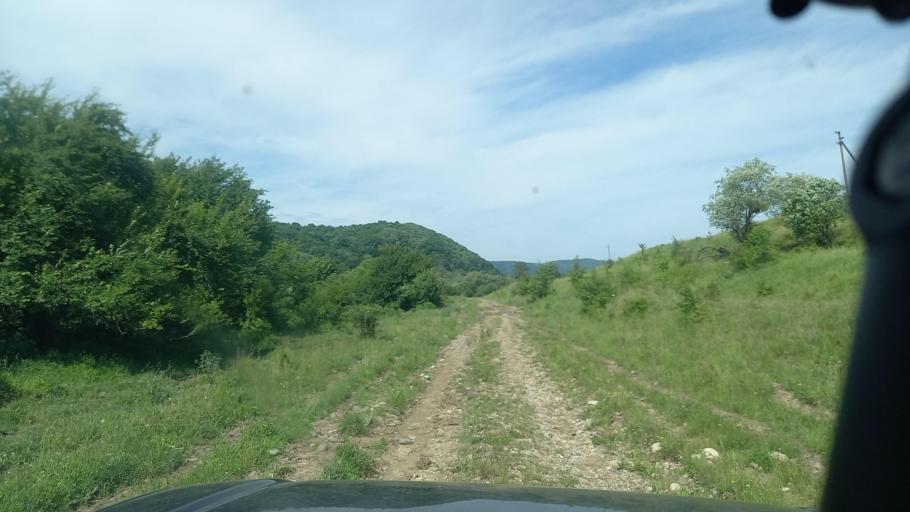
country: RU
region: Karachayevo-Cherkesiya
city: Kurdzhinovo
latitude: 44.1408
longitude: 41.0636
